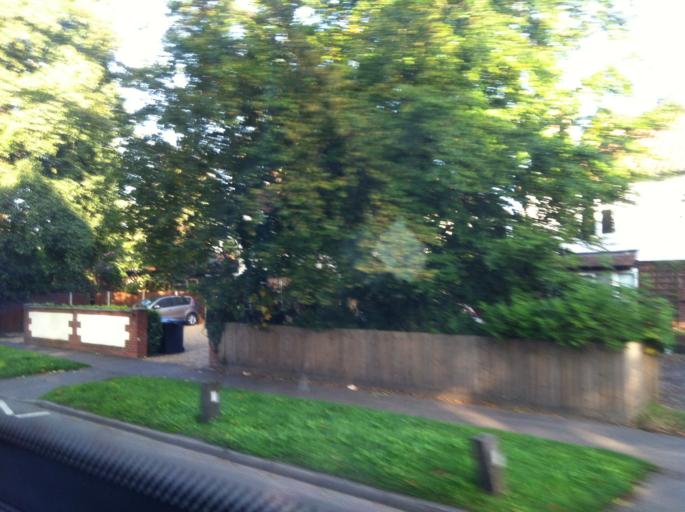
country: GB
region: England
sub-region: Norfolk
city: Cringleford
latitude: 52.6289
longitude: 1.2498
